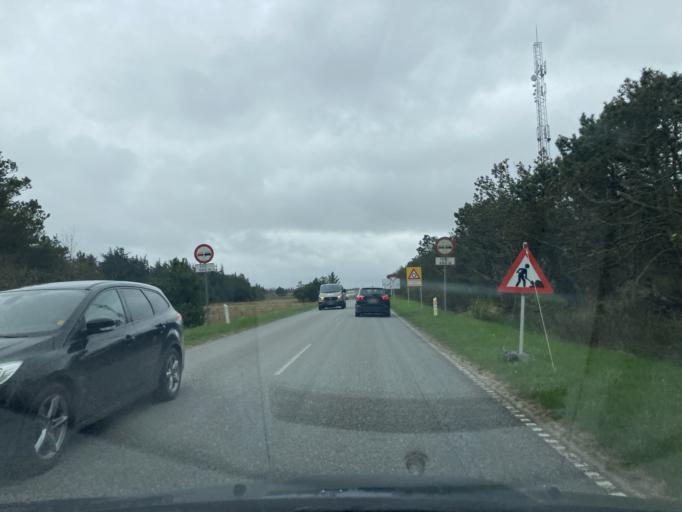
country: DK
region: North Denmark
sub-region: Thisted Kommune
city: Hurup
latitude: 56.9480
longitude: 8.3897
